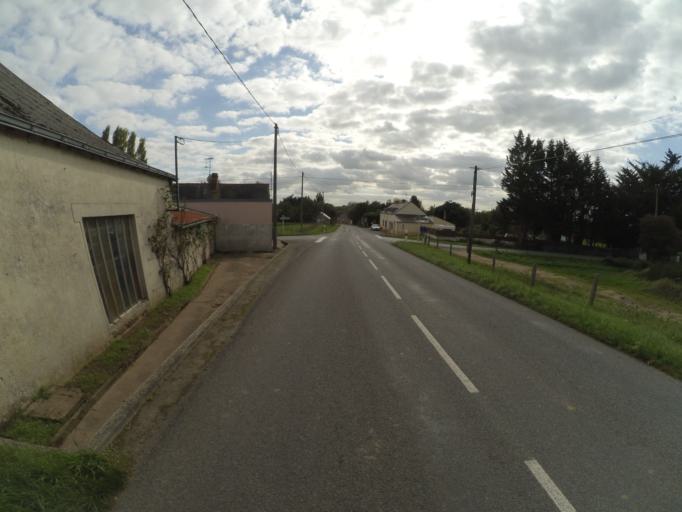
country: FR
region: Pays de la Loire
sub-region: Departement de la Loire-Atlantique
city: Bouvron
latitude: 47.4765
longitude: -1.8397
